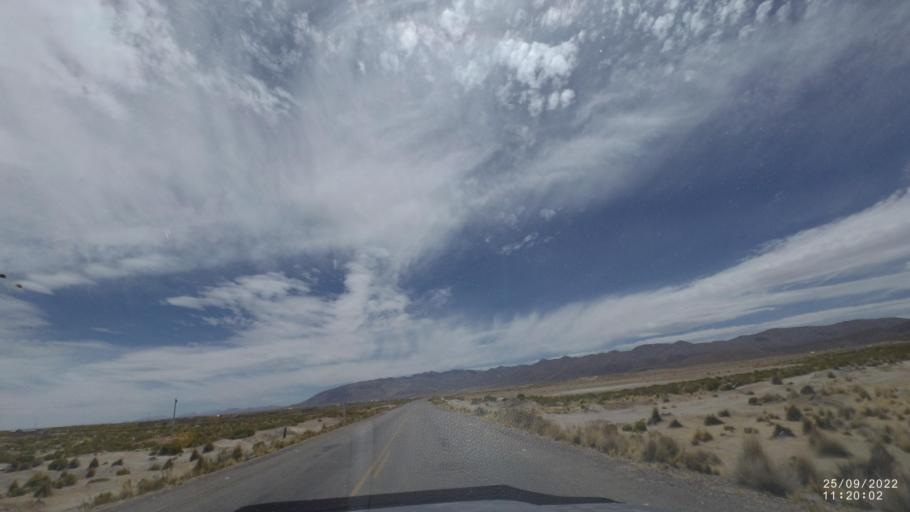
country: BO
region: Oruro
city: Challapata
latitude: -19.1658
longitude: -66.7786
